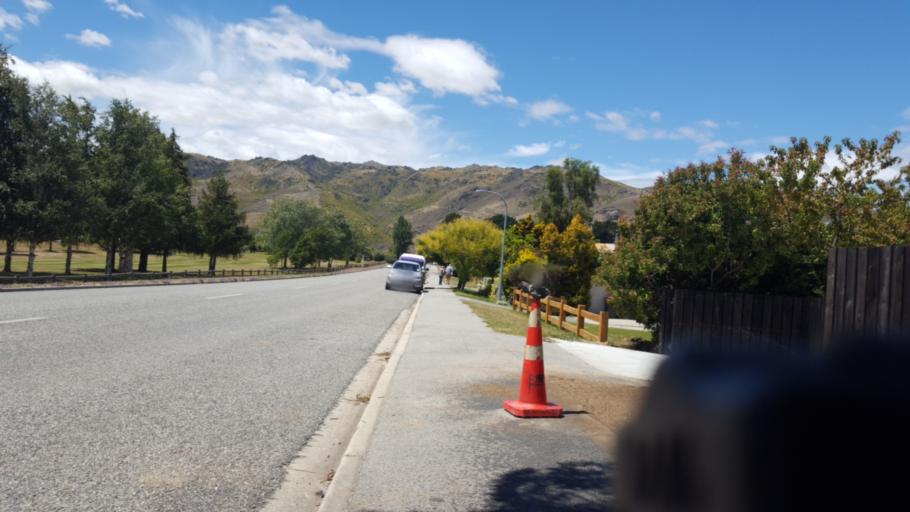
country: NZ
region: Otago
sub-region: Queenstown-Lakes District
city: Wanaka
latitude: -45.0406
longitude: 169.2046
